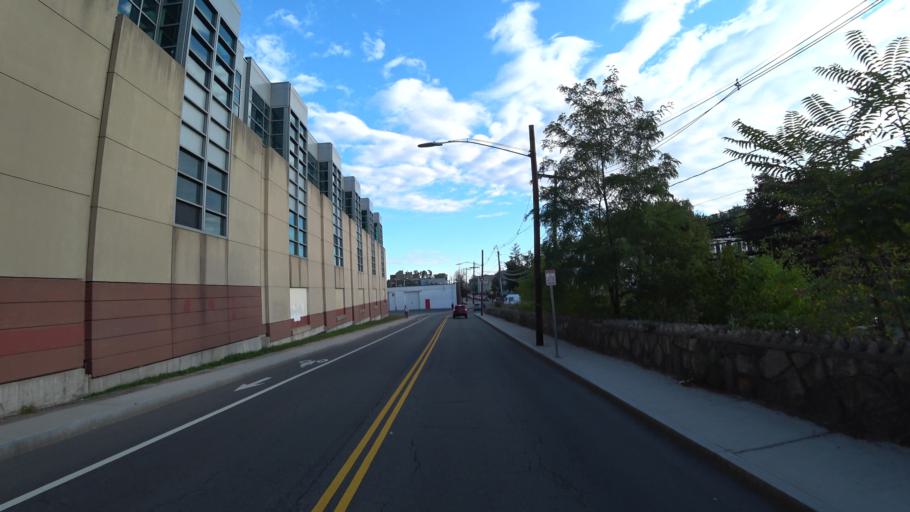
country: US
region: Massachusetts
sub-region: Norfolk County
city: Brookline
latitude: 42.3583
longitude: -71.1376
